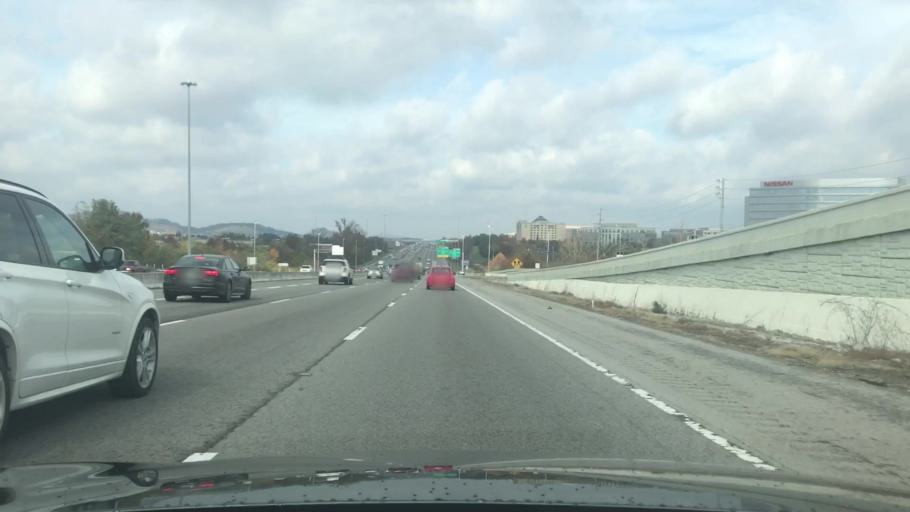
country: US
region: Tennessee
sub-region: Williamson County
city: Franklin
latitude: 35.9360
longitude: -86.8180
